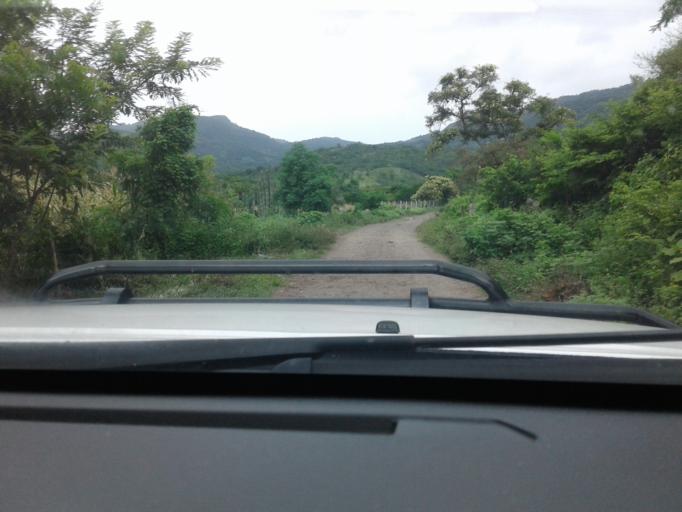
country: NI
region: Matagalpa
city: Ciudad Dario
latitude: 12.9021
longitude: -86.2066
